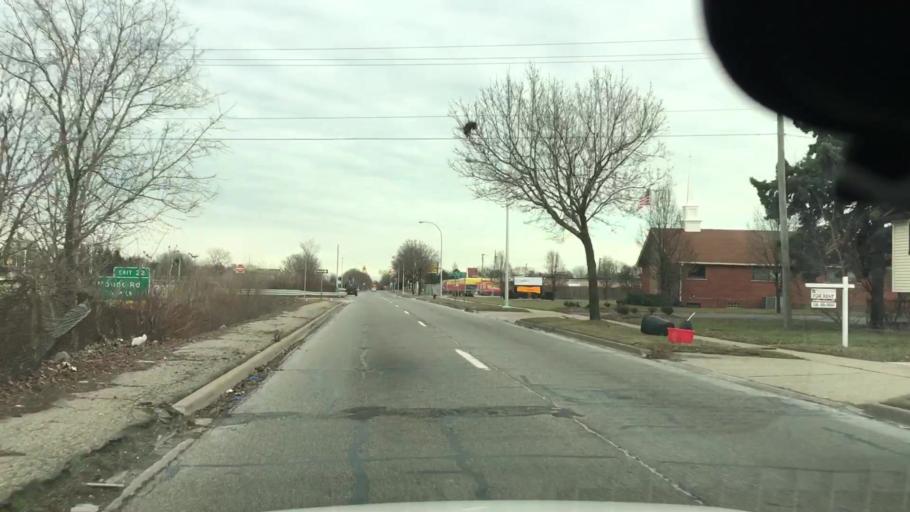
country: US
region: Michigan
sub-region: Oakland County
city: Madison Heights
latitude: 42.4907
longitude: -83.0697
